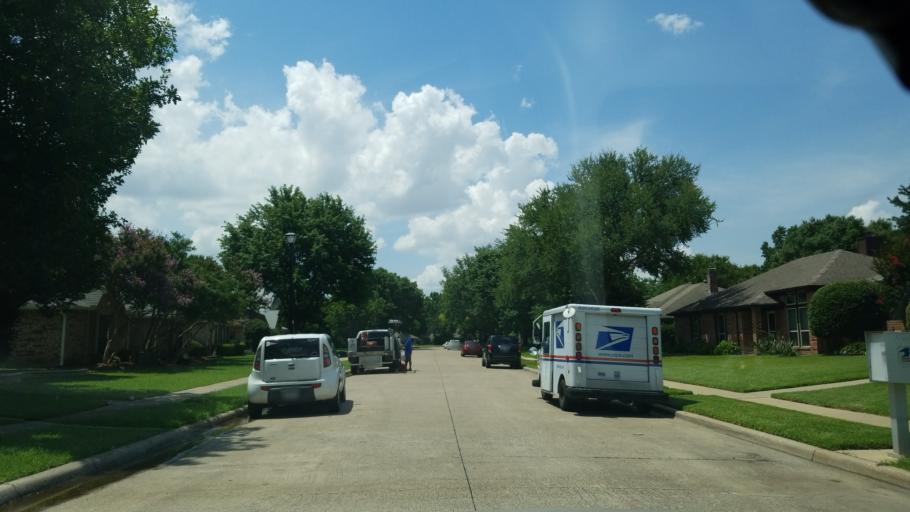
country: US
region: Texas
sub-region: Dallas County
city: Coppell
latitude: 32.9679
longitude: -96.9675
